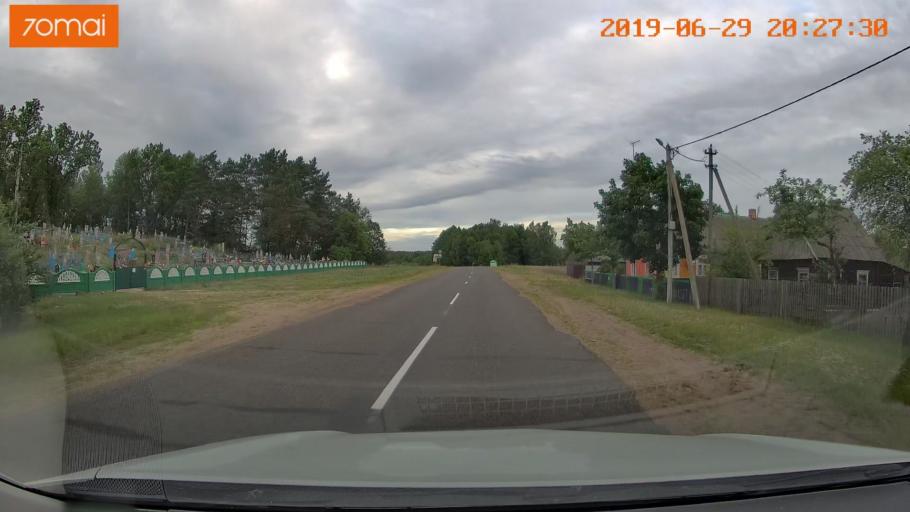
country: BY
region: Brest
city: Hantsavichy
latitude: 52.4741
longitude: 26.3049
